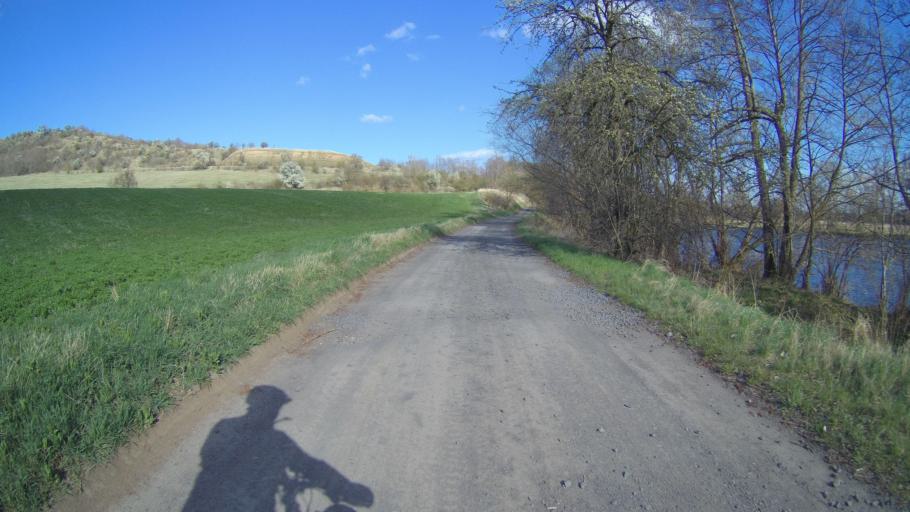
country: CZ
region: Ustecky
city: Brezno
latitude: 50.3588
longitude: 13.4752
